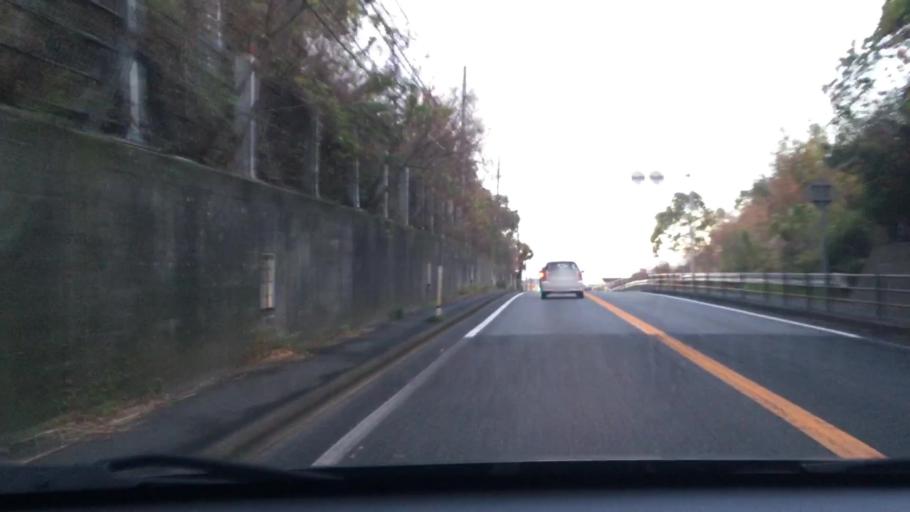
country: JP
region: Fukuoka
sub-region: Buzen-shi
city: Buzen
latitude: 33.6198
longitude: 131.0961
